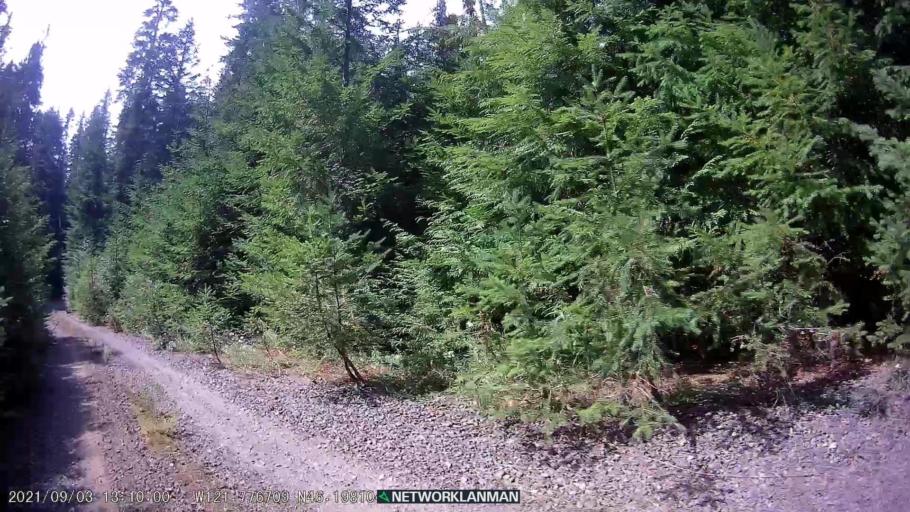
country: US
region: Washington
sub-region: Skamania County
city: Carson
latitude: 46.1981
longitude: -121.7767
